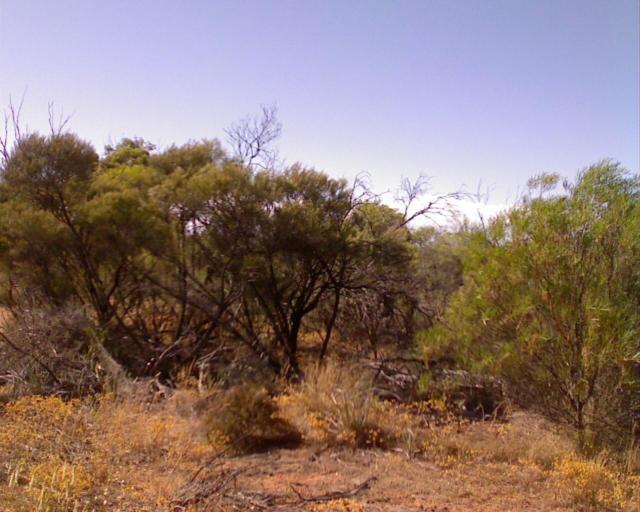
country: AU
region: Western Australia
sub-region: Moora
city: Moora
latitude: -29.8640
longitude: 116.1657
